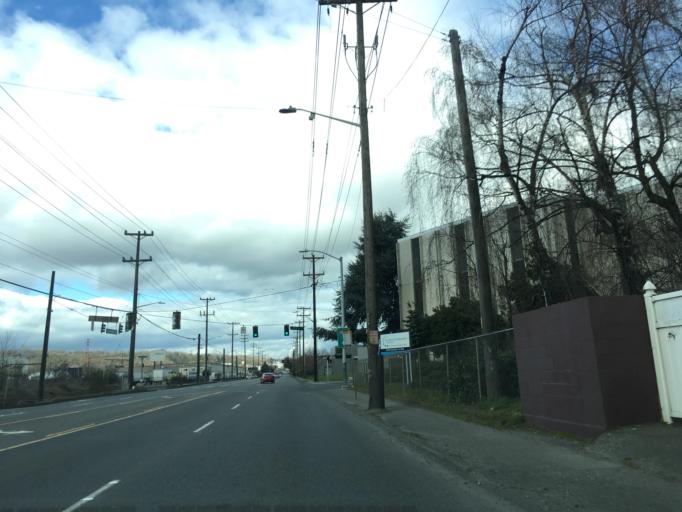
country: US
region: Washington
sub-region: King County
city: White Center
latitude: 47.5402
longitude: -122.3230
